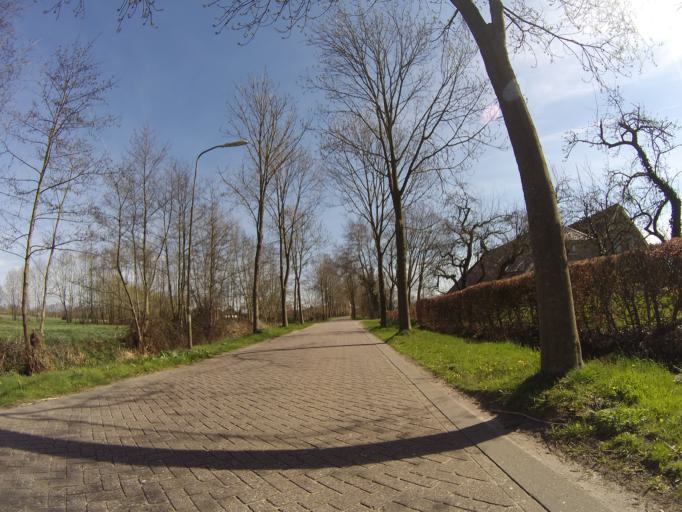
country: NL
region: Gelderland
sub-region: Gemeente Nijkerk
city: Nijkerk
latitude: 52.2087
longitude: 5.4879
